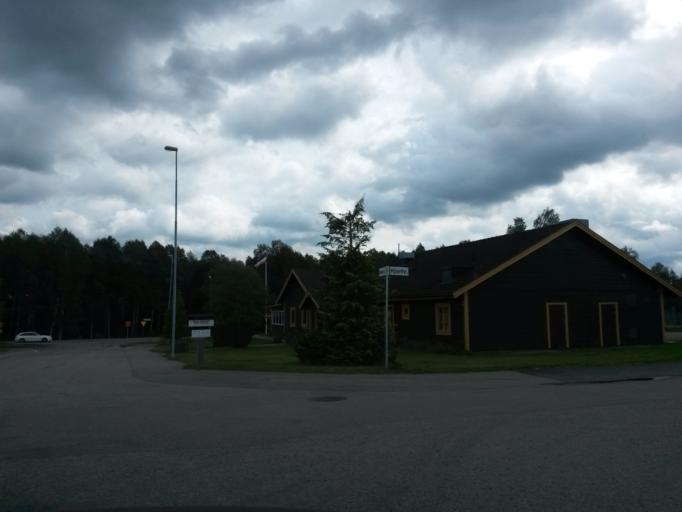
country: SE
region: Kronoberg
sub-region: Vaxjo Kommun
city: Vaexjoe
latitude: 56.9092
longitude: 14.8181
